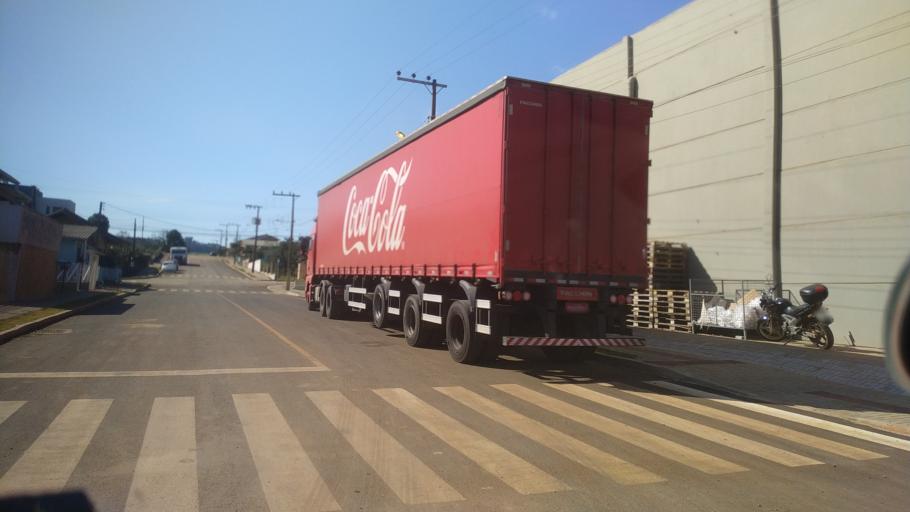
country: BR
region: Santa Catarina
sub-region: Chapeco
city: Chapeco
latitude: -27.0363
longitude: -52.6328
